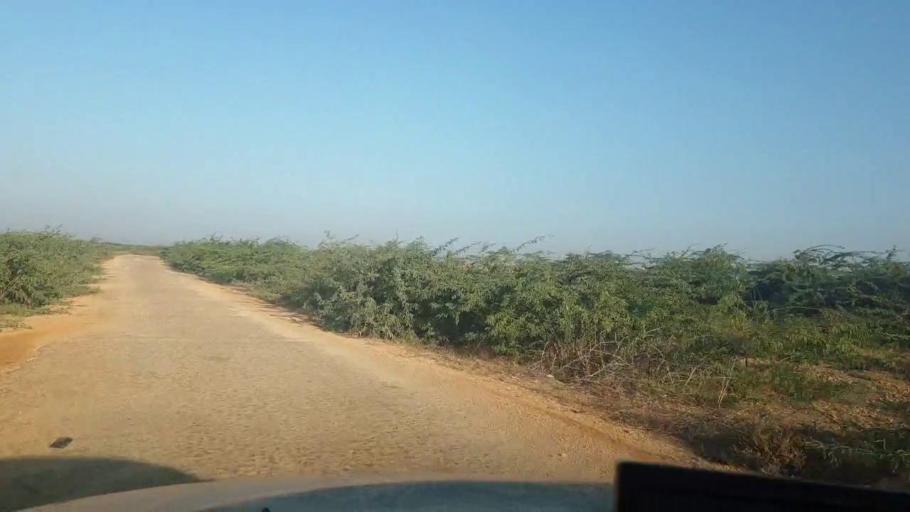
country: PK
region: Sindh
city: Thatta
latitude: 24.7064
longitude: 67.8485
